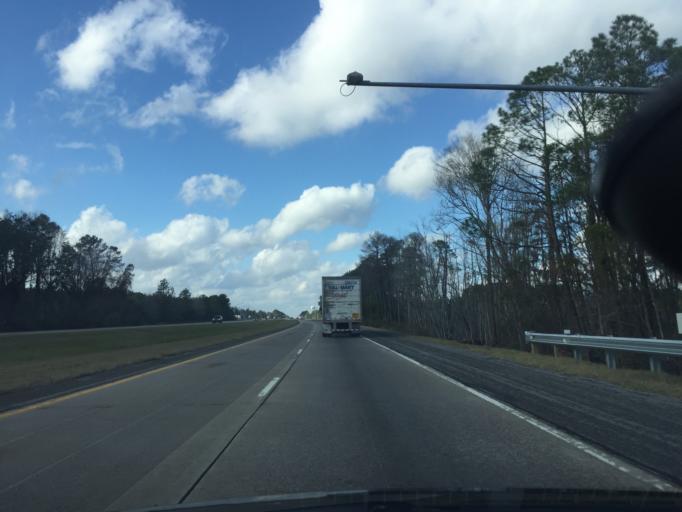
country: US
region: Georgia
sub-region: Chatham County
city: Bloomingdale
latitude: 32.1634
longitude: -81.4364
